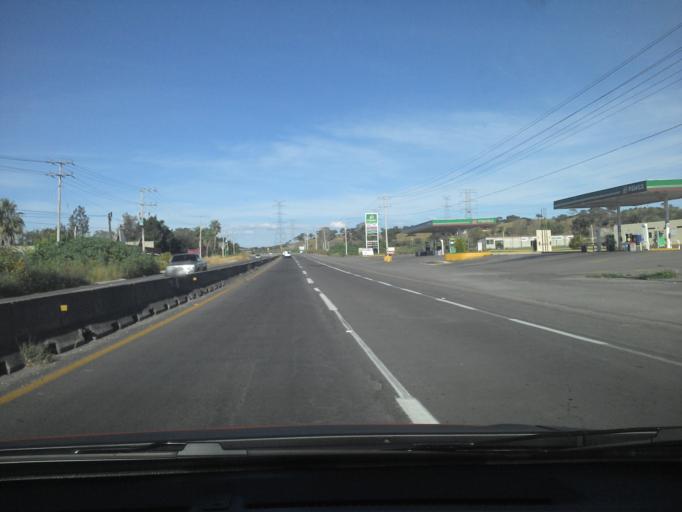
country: MX
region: Jalisco
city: Tala
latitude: 20.6800
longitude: -103.6984
